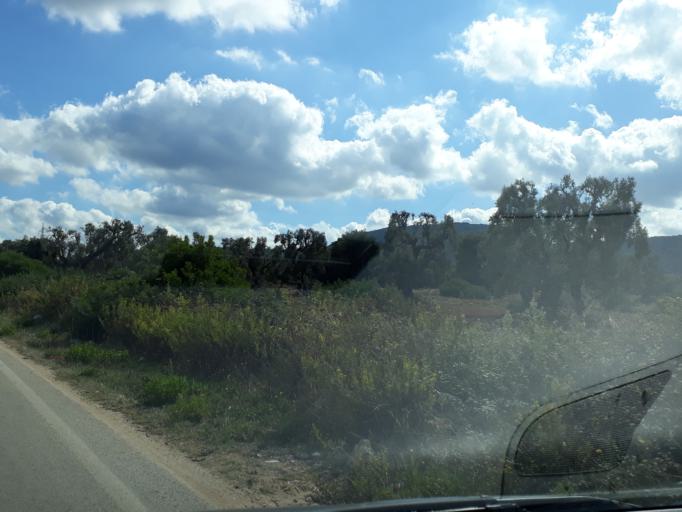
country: IT
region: Apulia
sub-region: Provincia di Brindisi
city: Pezze di Greco
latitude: 40.8003
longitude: 17.4028
